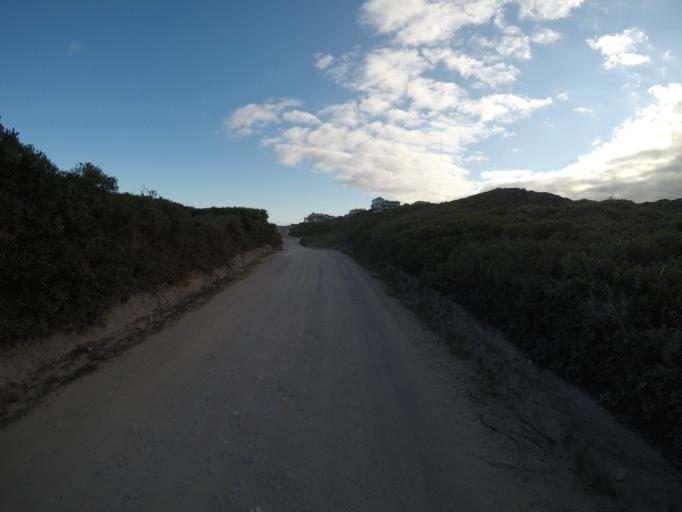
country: ZA
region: Western Cape
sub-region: Eden District Municipality
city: Riversdale
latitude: -34.4192
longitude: 21.3515
